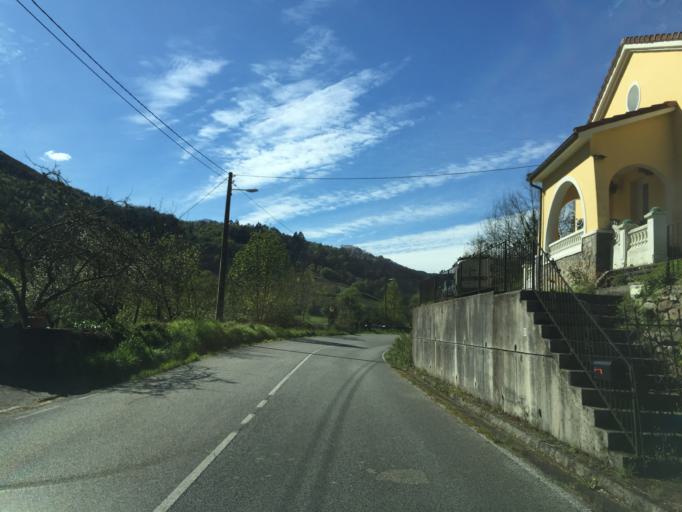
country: ES
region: Asturias
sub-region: Province of Asturias
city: Proaza
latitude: 43.3295
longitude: -5.9880
